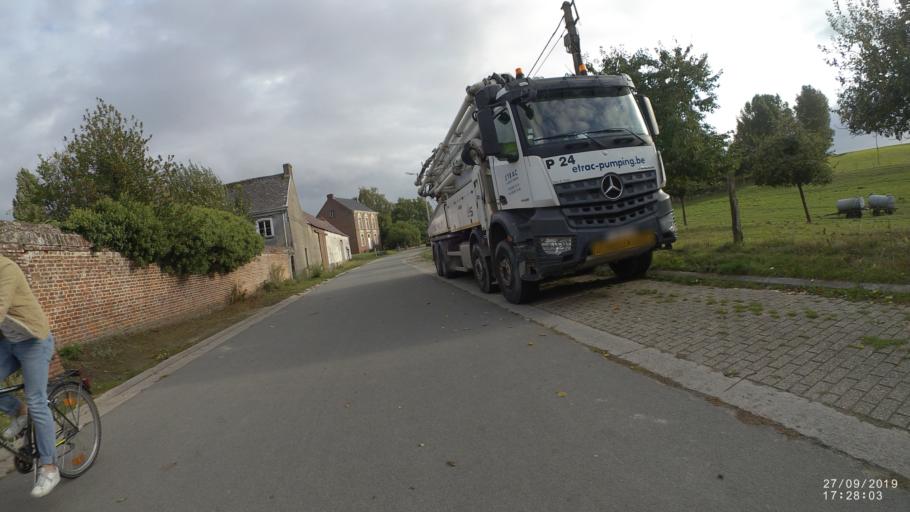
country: BE
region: Flanders
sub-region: Provincie Oost-Vlaanderen
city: Zottegem
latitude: 50.8523
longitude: 3.7859
